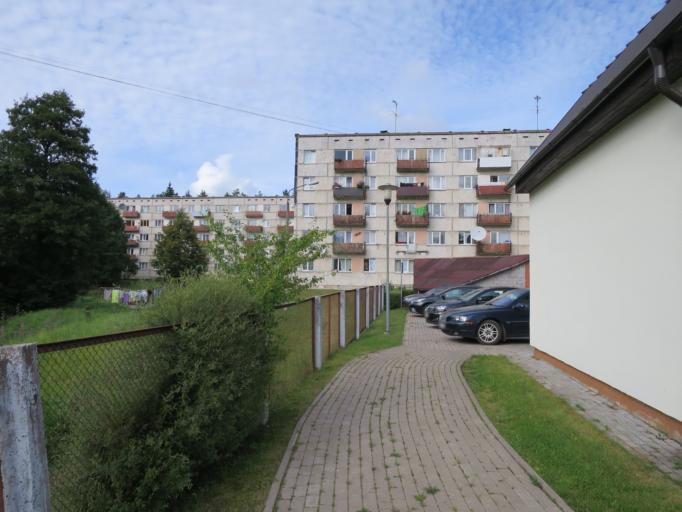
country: LV
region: Incukalns
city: Vangazi
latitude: 57.0954
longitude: 24.5427
